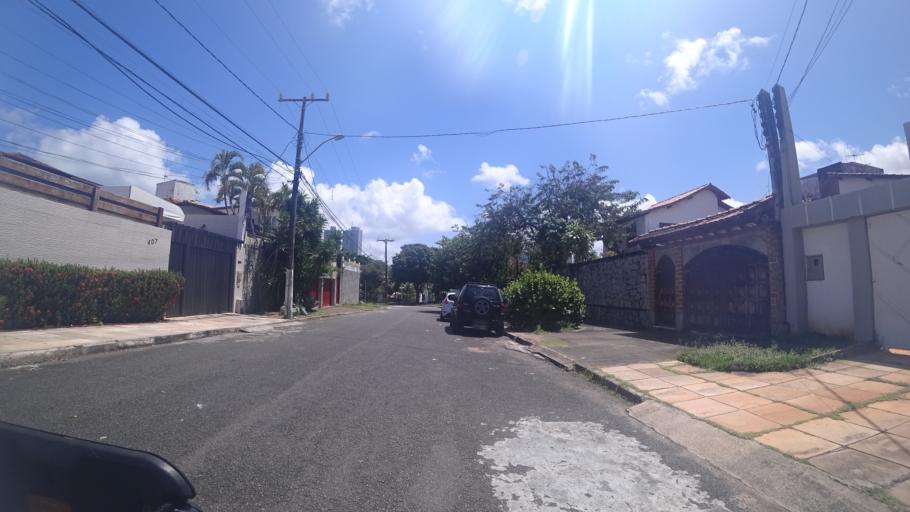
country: BR
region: Bahia
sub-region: Salvador
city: Salvador
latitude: -12.9924
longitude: -38.4679
